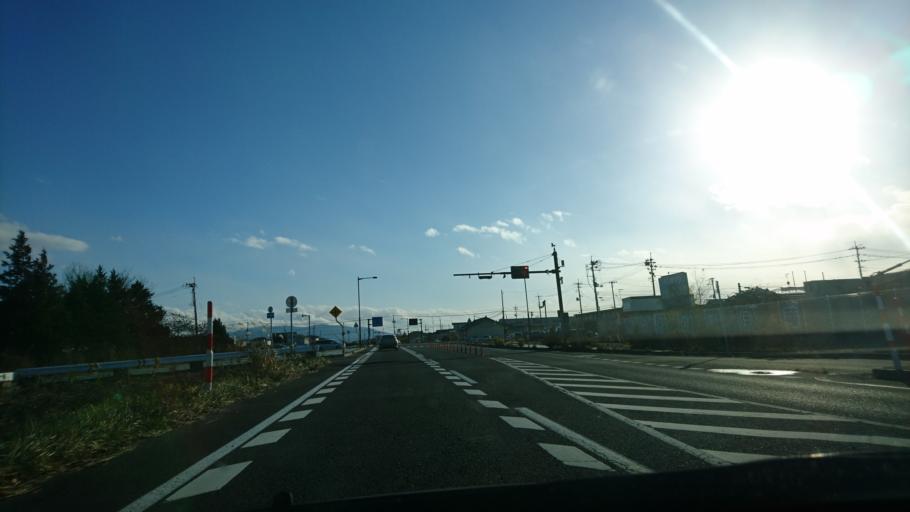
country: JP
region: Iwate
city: Mizusawa
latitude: 39.1378
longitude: 141.1627
